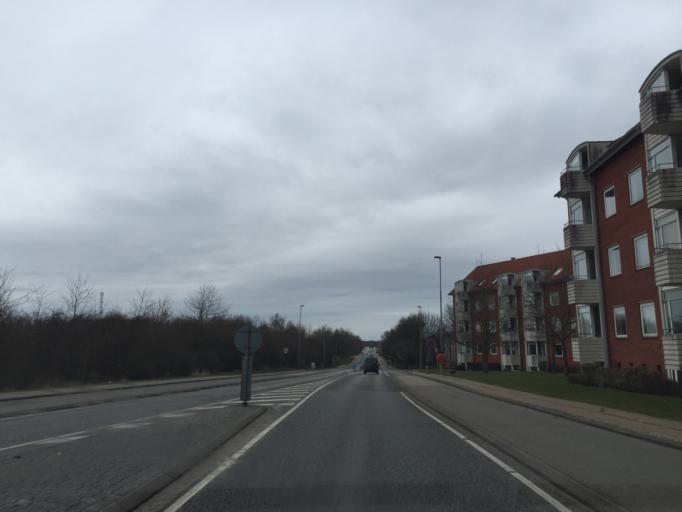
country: DK
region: South Denmark
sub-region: Odense Kommune
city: Odense
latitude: 55.3998
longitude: 10.3399
